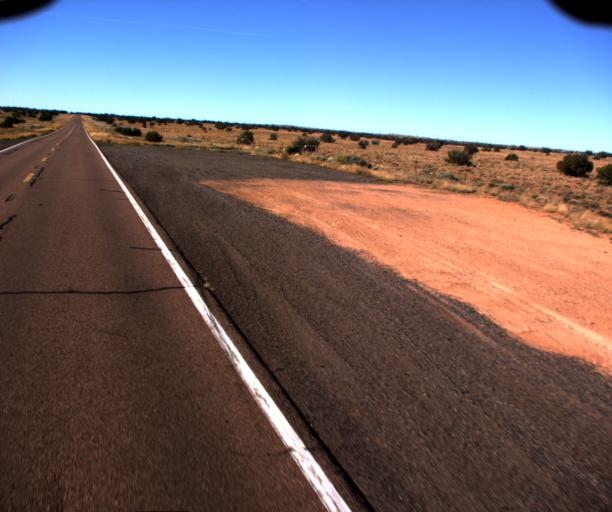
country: US
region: Arizona
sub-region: Navajo County
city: Holbrook
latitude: 34.7001
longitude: -110.3038
